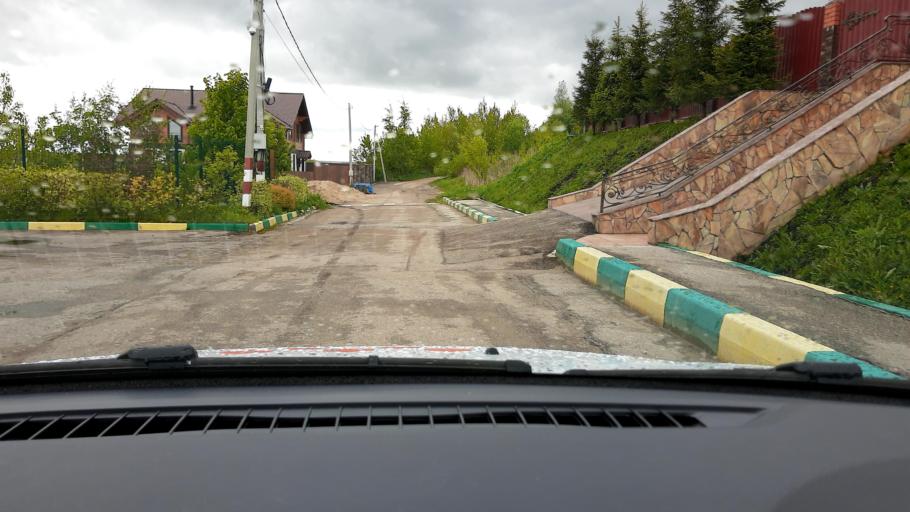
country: RU
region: Nizjnij Novgorod
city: Afonino
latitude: 56.2675
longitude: 44.0985
